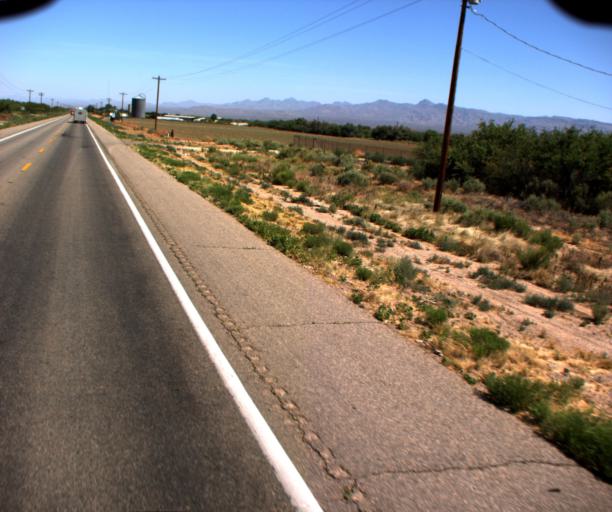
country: US
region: Arizona
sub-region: Graham County
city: Pima
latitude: 32.9521
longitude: -109.9145
